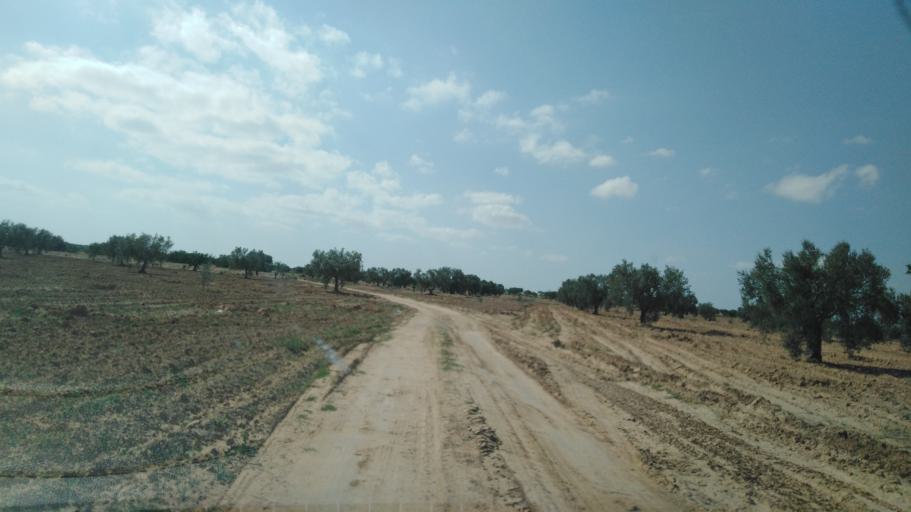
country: TN
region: Safaqis
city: Bi'r `Ali Bin Khalifah
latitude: 34.7986
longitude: 10.3863
